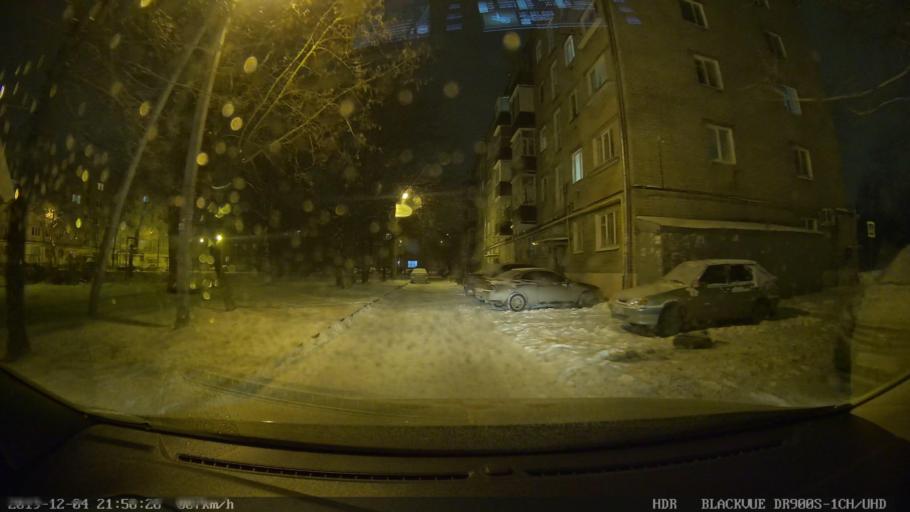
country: RU
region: Tatarstan
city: Staroye Arakchino
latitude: 55.8753
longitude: 49.0213
